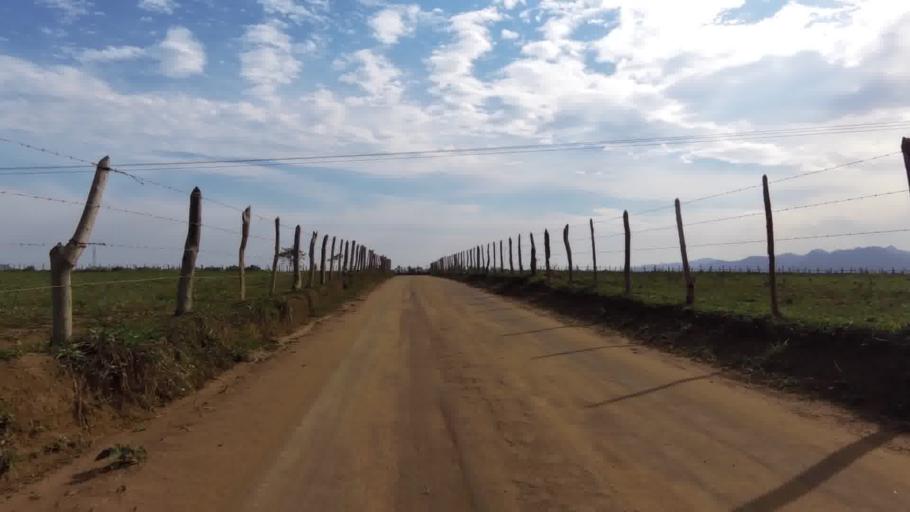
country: BR
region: Espirito Santo
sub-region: Piuma
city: Piuma
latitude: -20.8226
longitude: -40.7463
